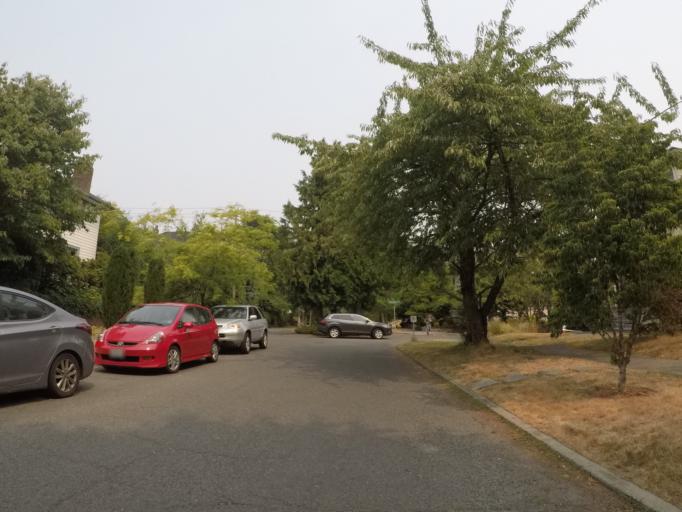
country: US
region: Washington
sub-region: King County
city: Seattle
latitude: 47.6218
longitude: -122.3087
